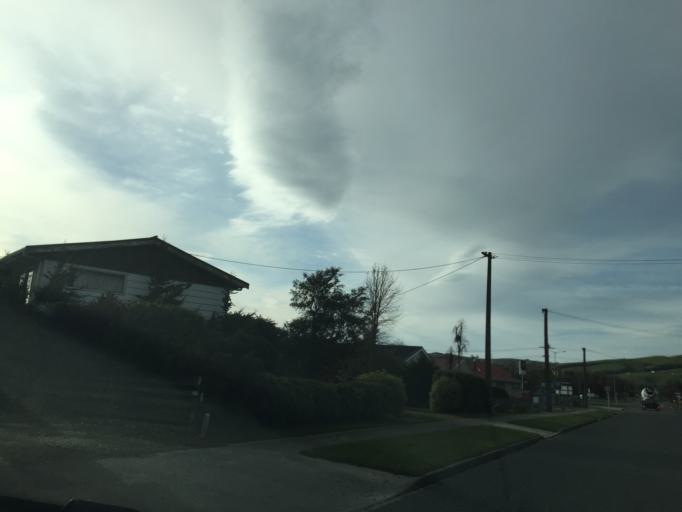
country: NZ
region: Southland
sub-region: Gore District
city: Gore
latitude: -46.1141
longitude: 168.9326
